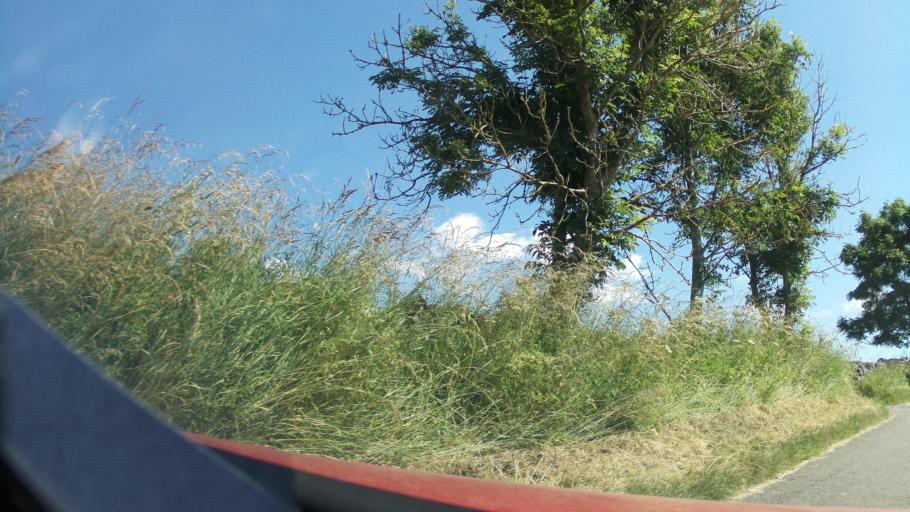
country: GB
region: England
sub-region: Derbyshire
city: Buxton
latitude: 53.2849
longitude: -1.8571
